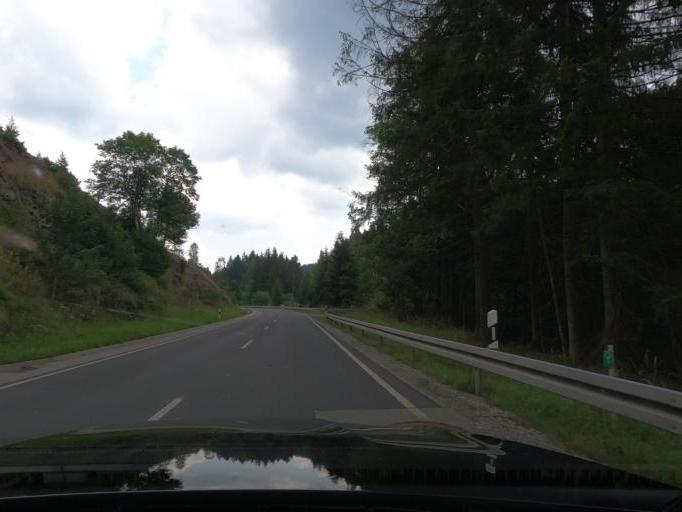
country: DE
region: Lower Saxony
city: Wildemann
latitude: 51.8077
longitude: 10.2828
